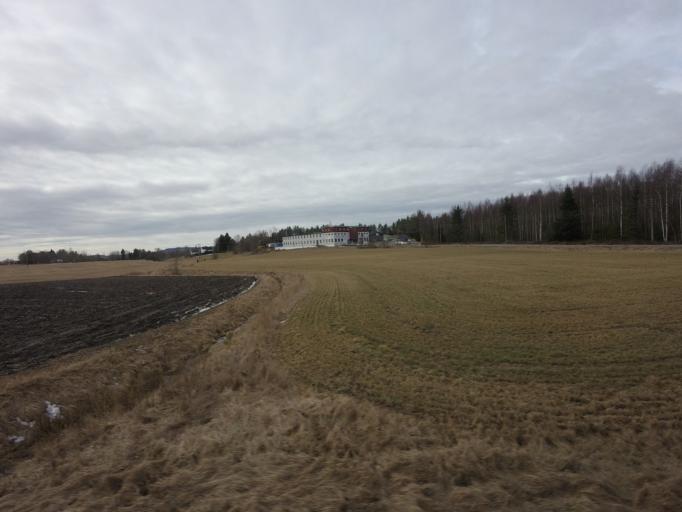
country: NO
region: Akershus
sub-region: Fet
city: Fetsund
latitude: 59.8979
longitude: 11.1911
